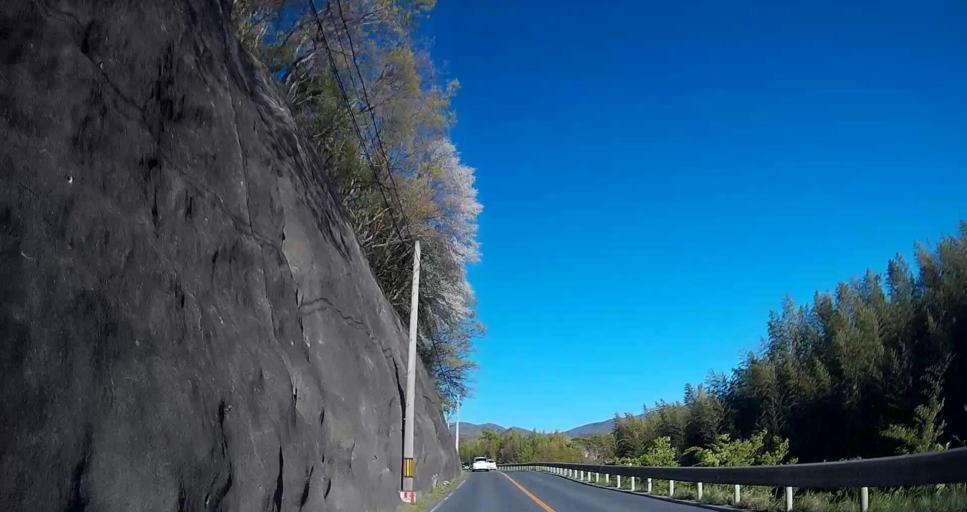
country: JP
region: Miyagi
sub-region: Oshika Gun
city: Onagawa Cho
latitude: 38.4366
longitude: 141.4020
